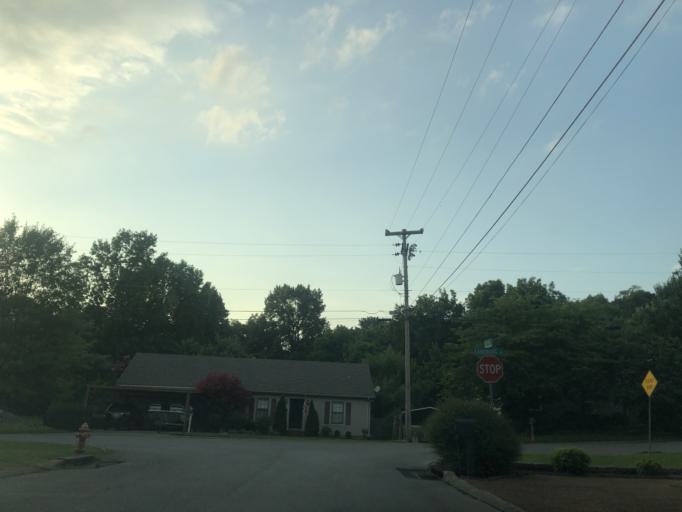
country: US
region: Tennessee
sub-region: Davidson County
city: Lakewood
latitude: 36.1400
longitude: -86.6322
